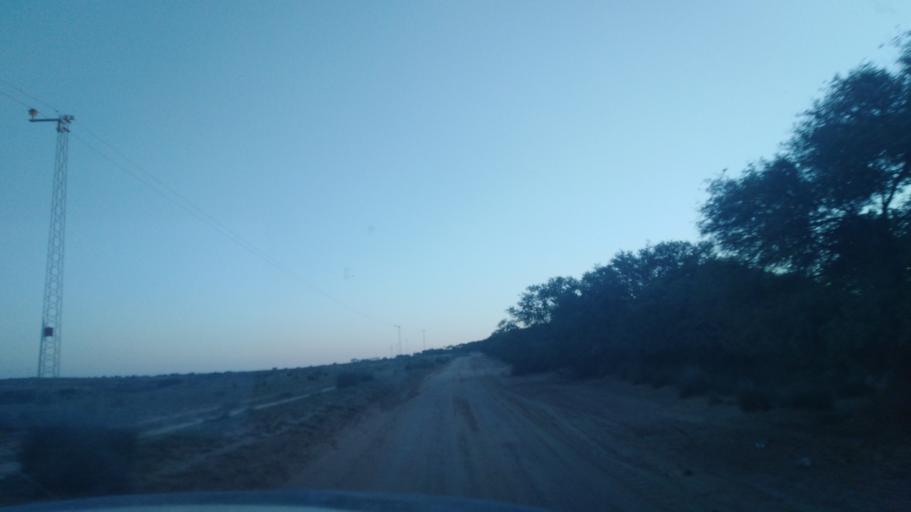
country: TN
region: Safaqis
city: Sfax
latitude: 34.7358
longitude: 10.4450
